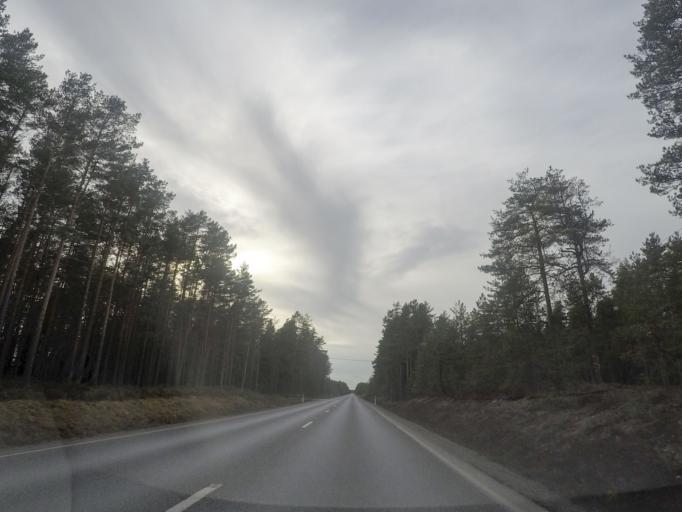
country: SE
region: Vaestmanland
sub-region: Surahammars Kommun
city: Ramnas
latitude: 59.7774
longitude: 16.0931
